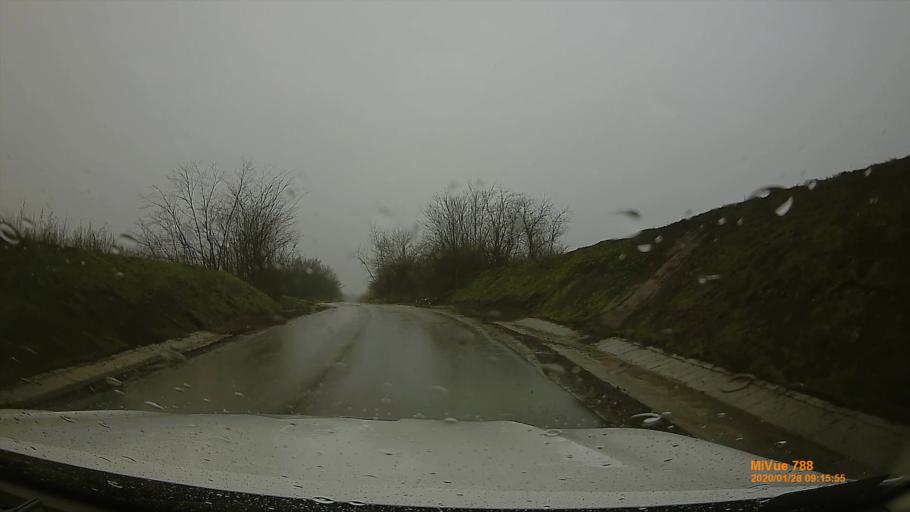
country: HU
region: Pest
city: Pilis
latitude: 47.2956
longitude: 19.5714
